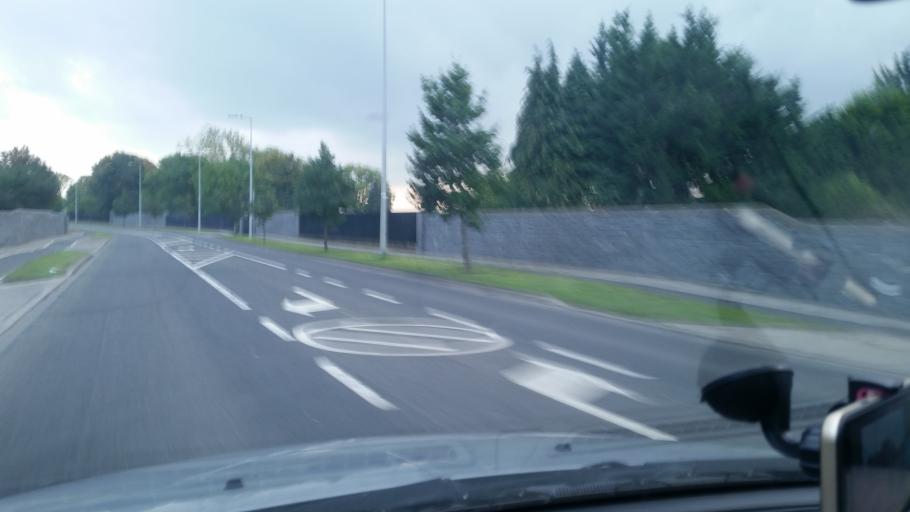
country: IE
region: Leinster
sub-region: Fingal County
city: Blanchardstown
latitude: 53.4003
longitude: -6.3533
